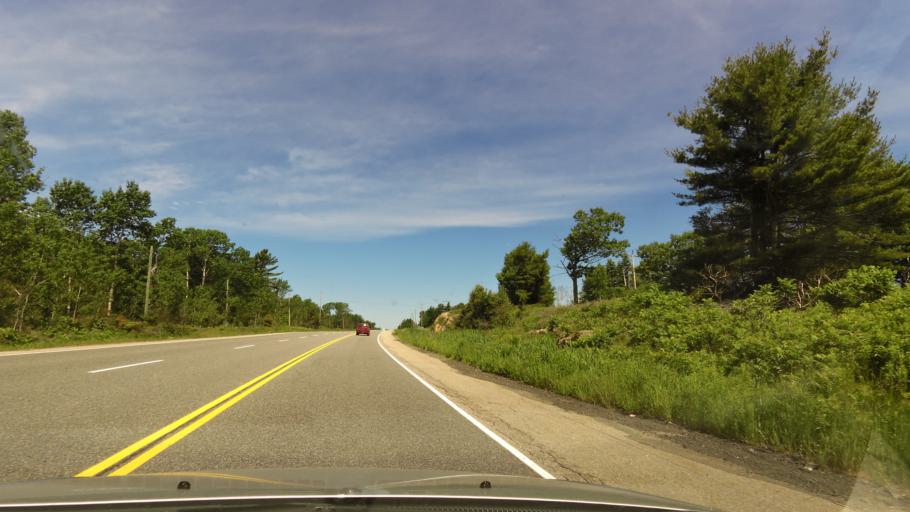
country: CA
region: Ontario
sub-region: Parry Sound District
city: Parry Sound
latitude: 45.5779
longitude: -80.3545
